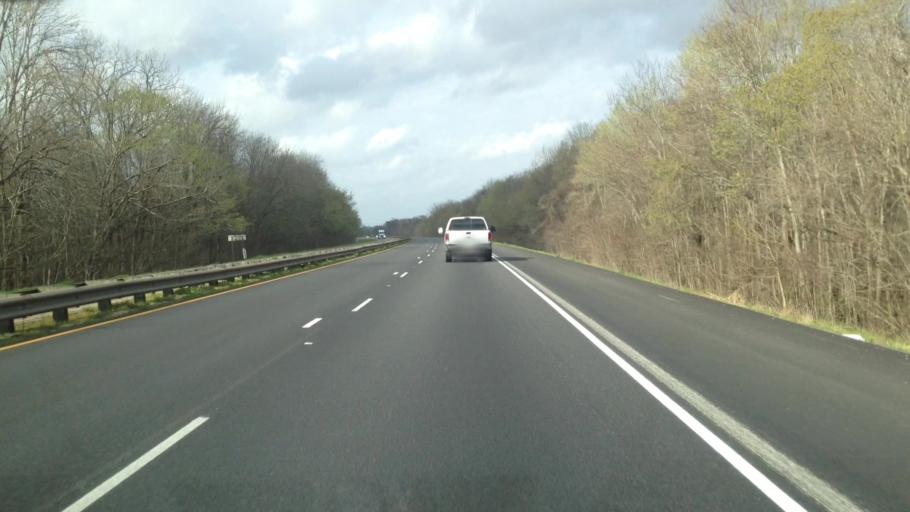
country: US
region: Louisiana
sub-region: Saint Landry Parish
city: Krotz Springs
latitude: 30.5515
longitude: -91.7322
